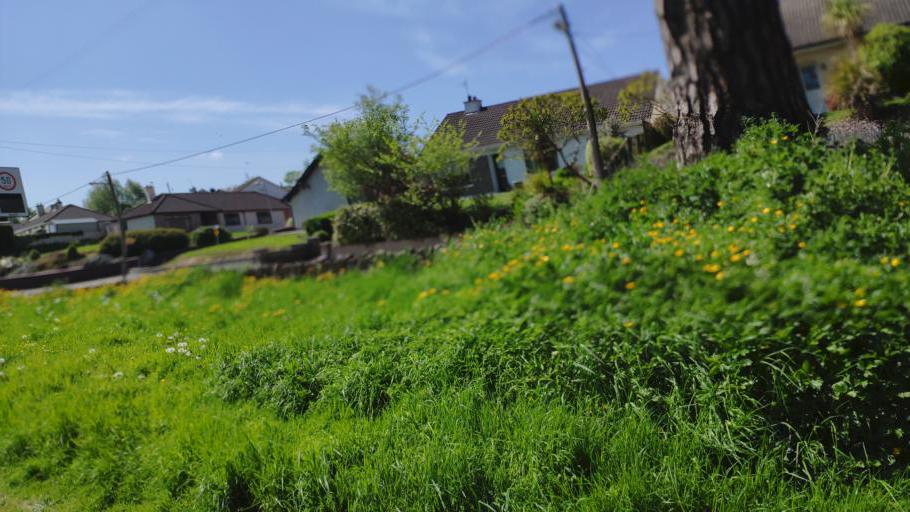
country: IE
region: Munster
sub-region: County Cork
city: Blarney
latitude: 51.9378
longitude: -8.5634
